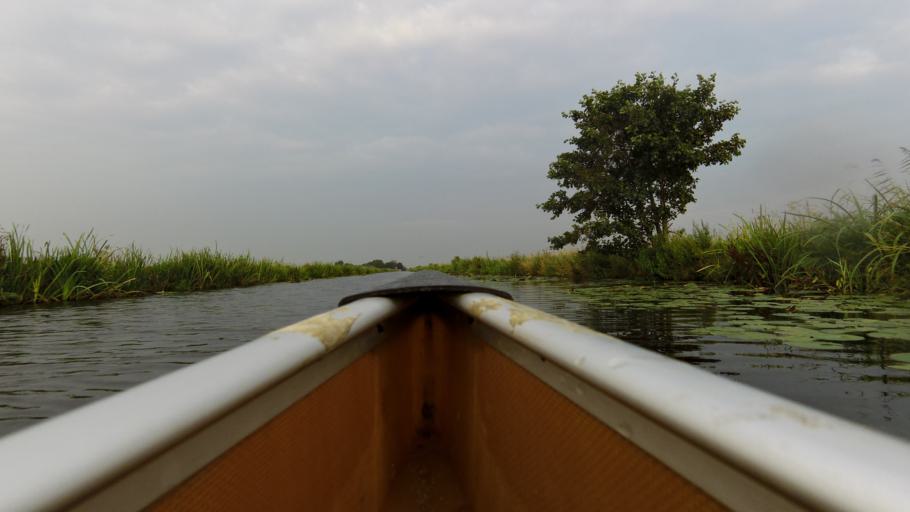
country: NL
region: South Holland
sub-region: Gemeente Leiderdorp
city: Leiderdorp
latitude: 52.1933
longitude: 4.5482
